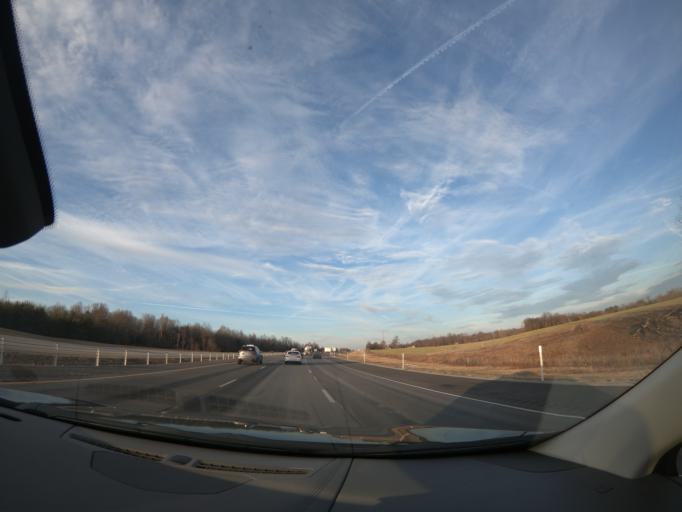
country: US
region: Kentucky
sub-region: Hardin County
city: Elizabethtown
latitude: 37.7209
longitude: -85.8276
